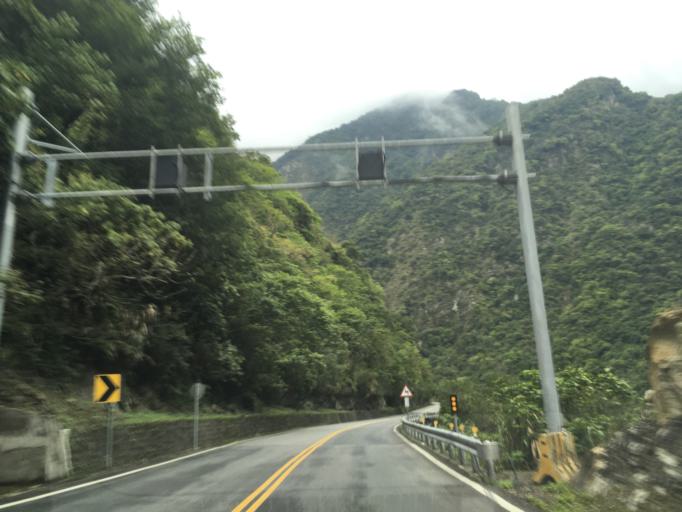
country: TW
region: Taiwan
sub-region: Hualien
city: Hualian
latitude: 24.1728
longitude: 121.5871
